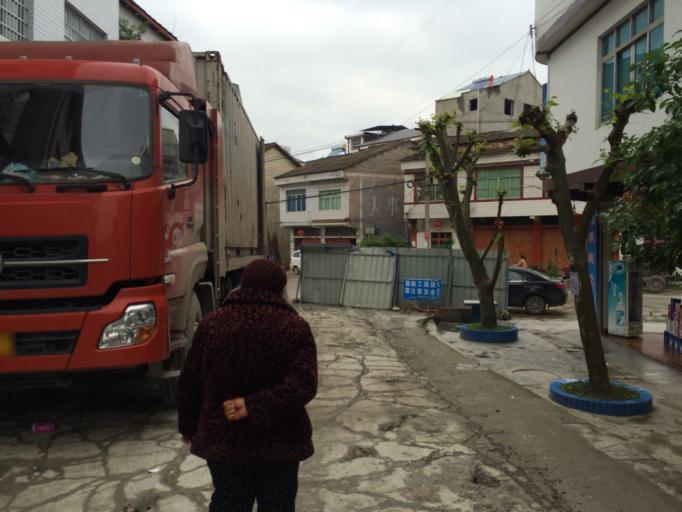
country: CN
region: Guizhou Sheng
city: Dalucao
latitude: 27.8341
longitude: 107.2529
